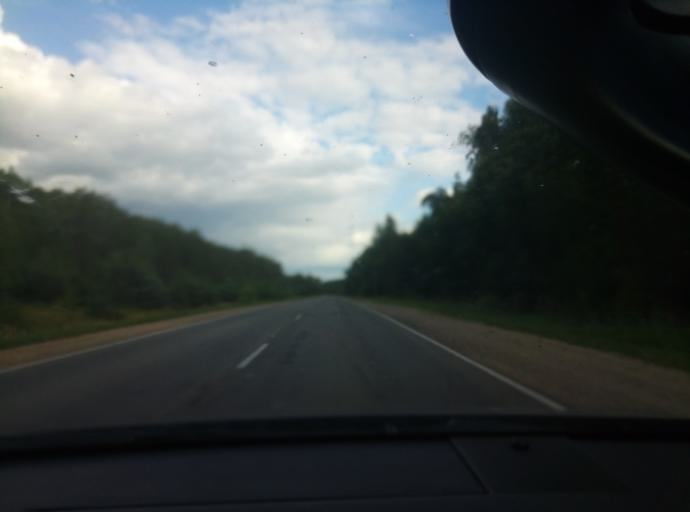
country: RU
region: Kaluga
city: Nikola-Lenivets
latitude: 54.5388
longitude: 35.5497
